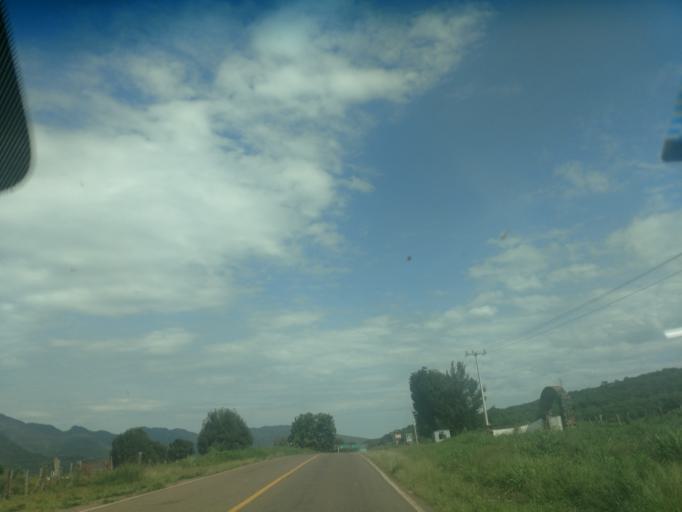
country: MX
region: Jalisco
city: Talpa de Allende
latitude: 20.4405
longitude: -104.7513
